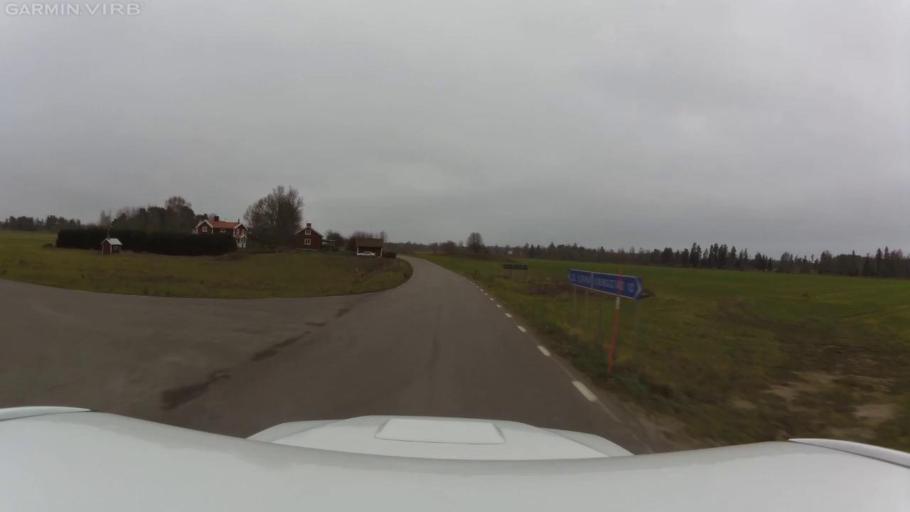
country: SE
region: OEstergoetland
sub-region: Linkopings Kommun
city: Vikingstad
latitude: 58.3052
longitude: 15.3808
